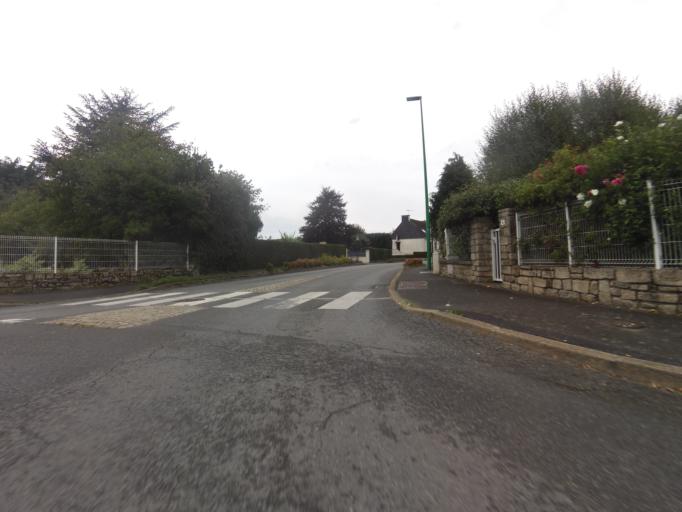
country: FR
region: Brittany
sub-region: Departement du Morbihan
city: Saint-Ave
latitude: 47.6959
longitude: -2.7469
